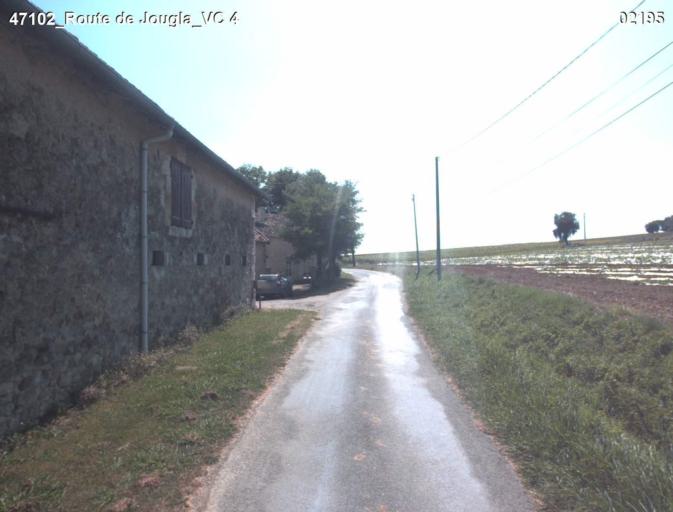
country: FR
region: Aquitaine
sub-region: Departement du Lot-et-Garonne
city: Nerac
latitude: 44.0595
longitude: 0.4303
